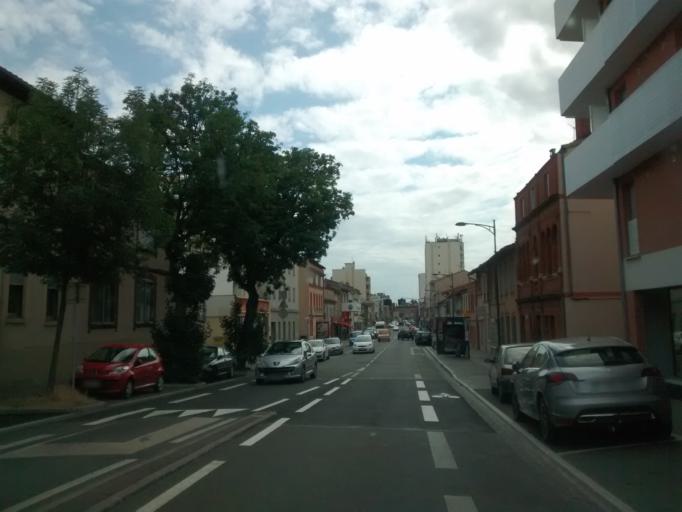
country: FR
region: Midi-Pyrenees
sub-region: Departement de la Haute-Garonne
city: Toulouse
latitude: 43.6234
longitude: 1.4589
